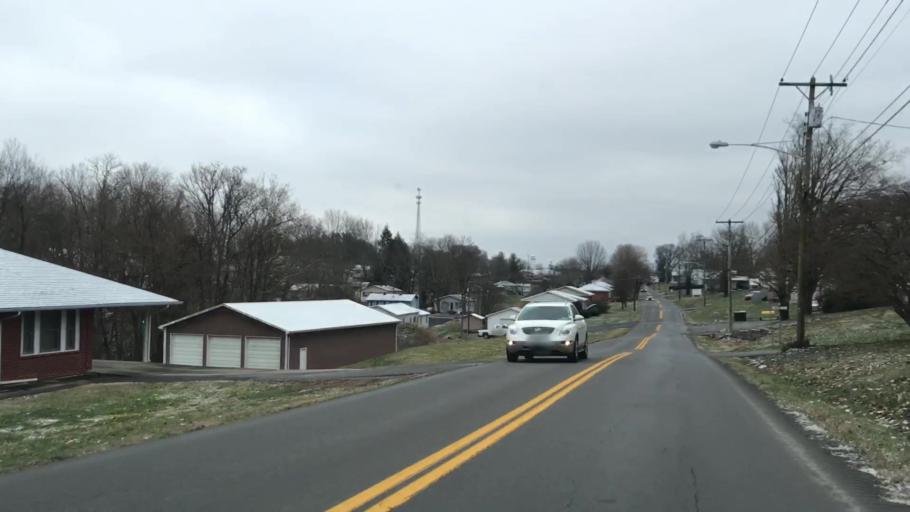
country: US
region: Kentucky
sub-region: Adair County
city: Columbia
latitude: 37.0956
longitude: -85.3093
